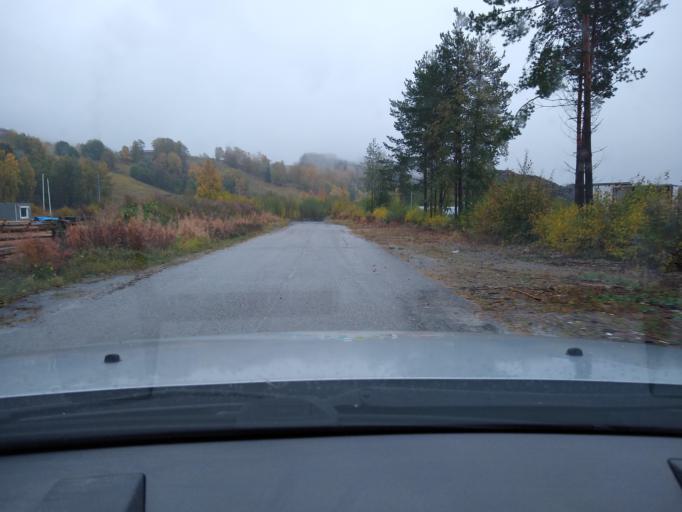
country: NO
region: Oppland
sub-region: Ringebu
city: Ringebu
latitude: 61.5474
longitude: 10.0674
